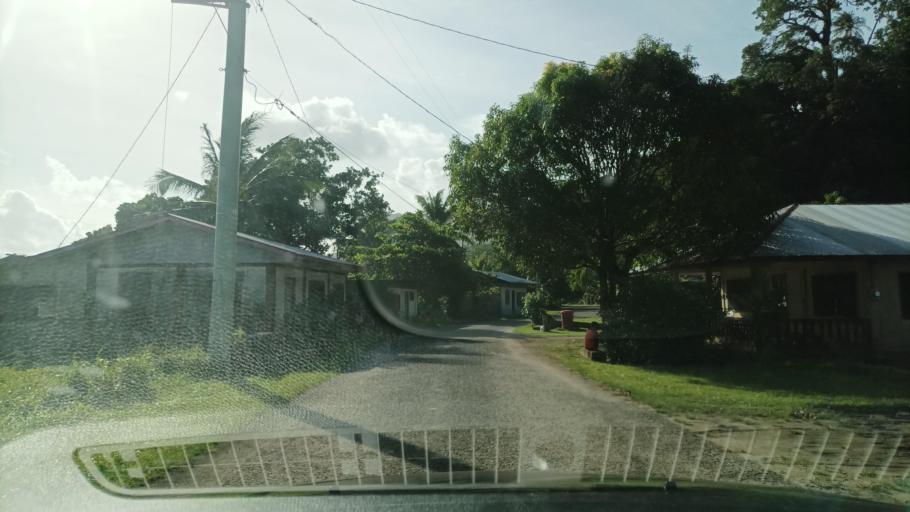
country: FM
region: Kosrae
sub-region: Lelu Municipality
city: Lelu
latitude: 5.3278
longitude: 163.0290
